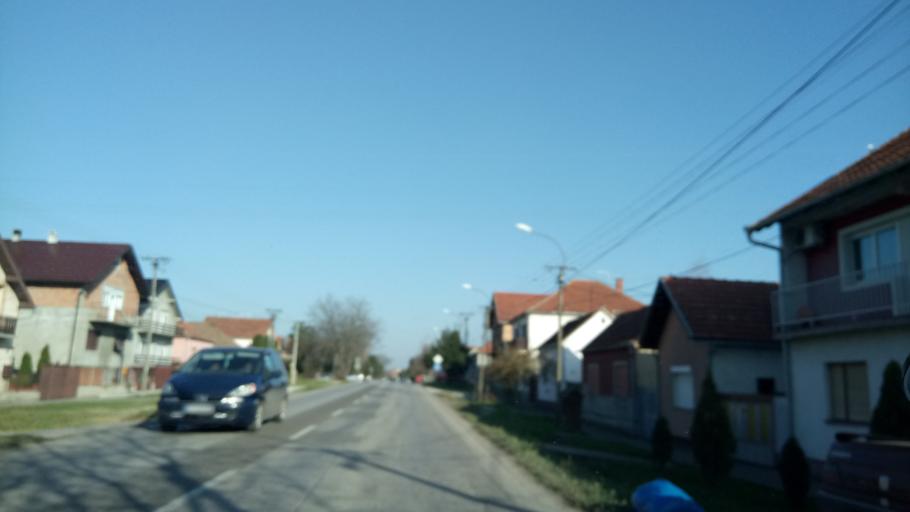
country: RS
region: Autonomna Pokrajina Vojvodina
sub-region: Sremski Okrug
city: Ingija
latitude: 45.0400
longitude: 20.0685
